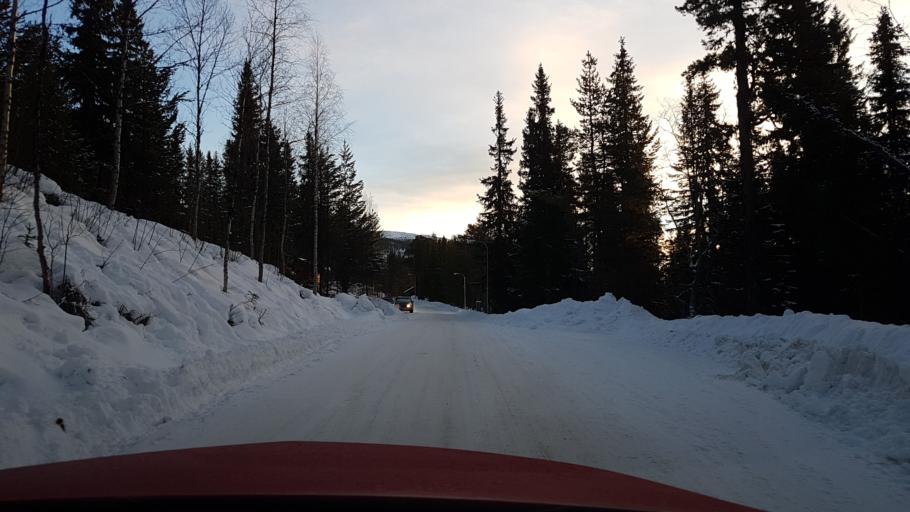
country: SE
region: Jaemtland
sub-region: Harjedalens Kommun
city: Sveg
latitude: 62.4253
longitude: 13.9446
